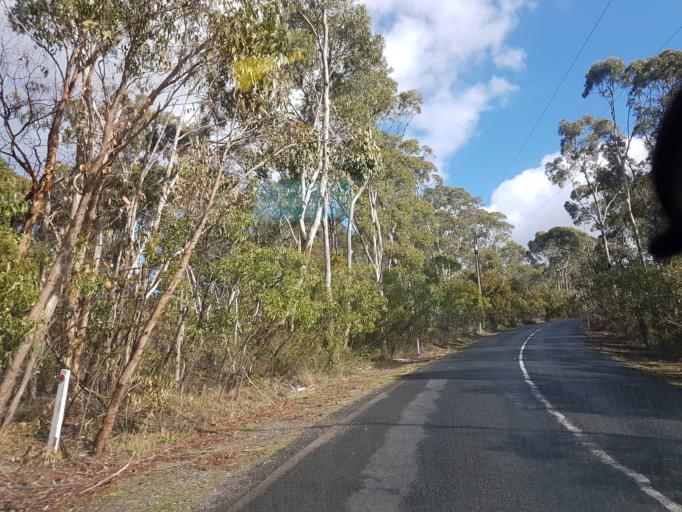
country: AU
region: South Australia
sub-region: Adelaide Hills
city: Heathfield
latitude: -35.0453
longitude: 138.7034
